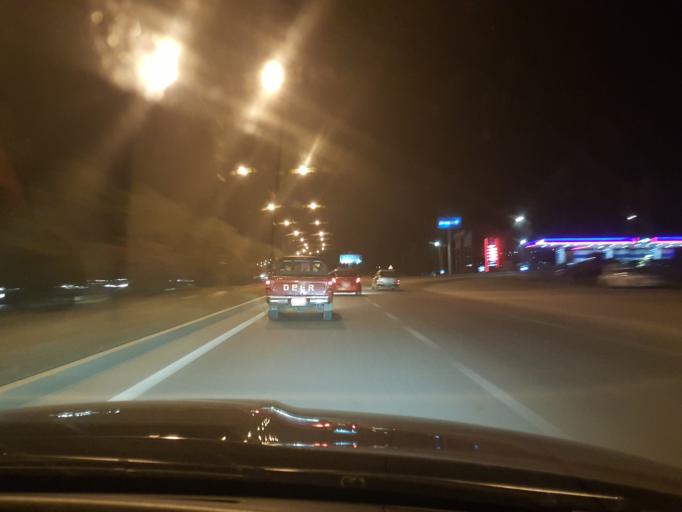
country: IQ
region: Arbil
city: Erbil
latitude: 36.2626
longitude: 44.0898
